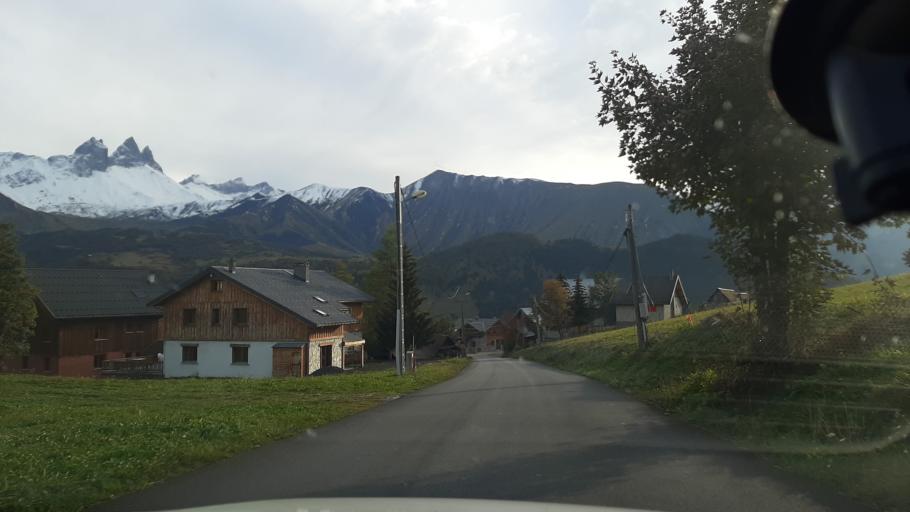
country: FR
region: Rhone-Alpes
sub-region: Departement de la Savoie
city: Villargondran
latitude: 45.2082
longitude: 6.3351
